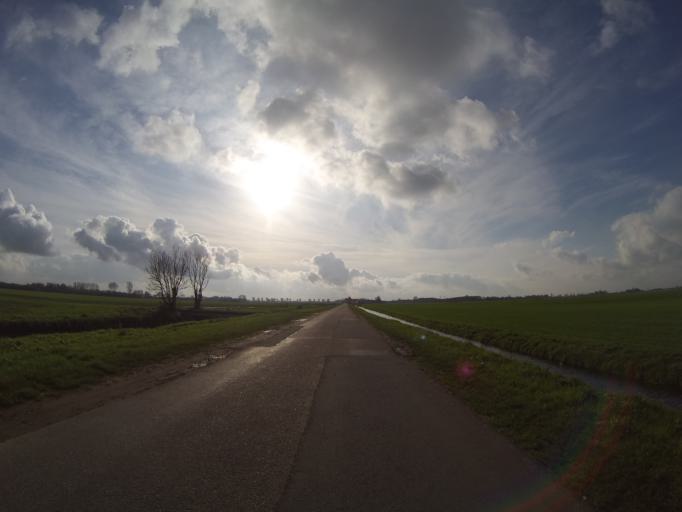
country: NL
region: Utrecht
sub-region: Gemeente Bunschoten
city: Bunschoten
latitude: 52.2333
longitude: 5.4273
